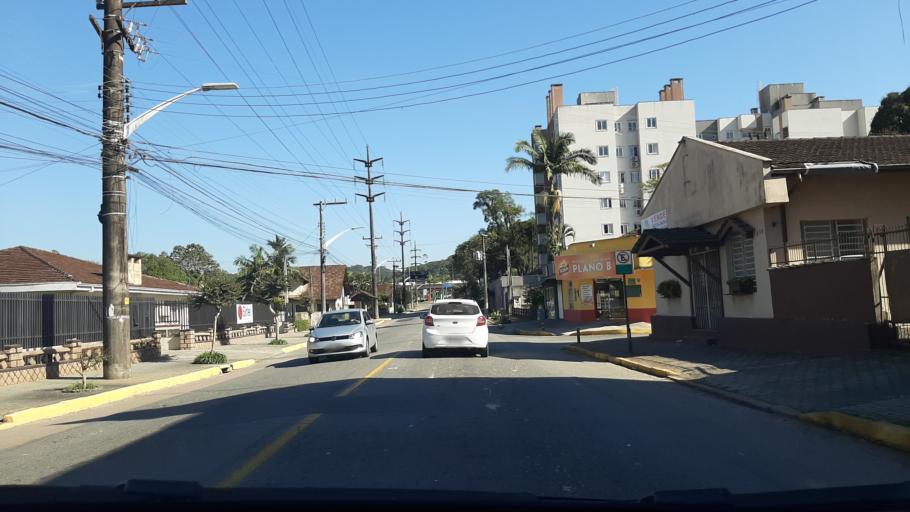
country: BR
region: Santa Catarina
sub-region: Joinville
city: Joinville
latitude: -26.3187
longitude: -48.8685
